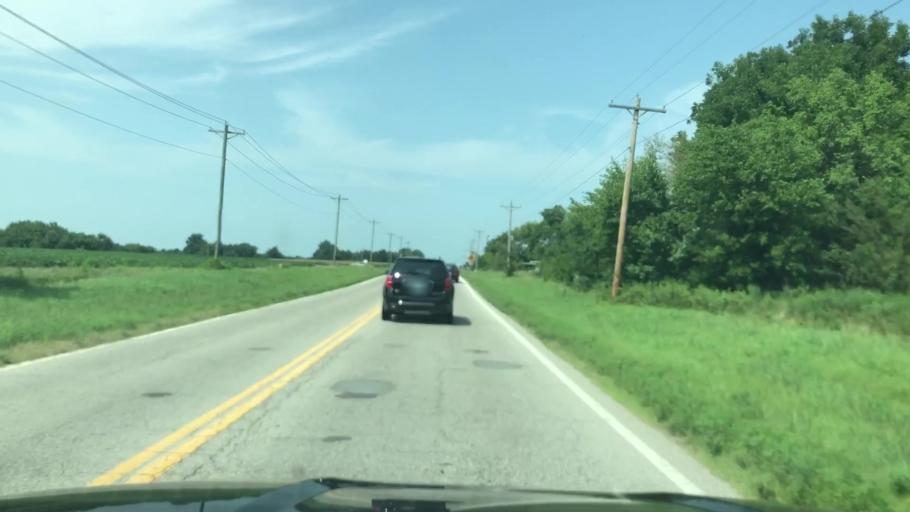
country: US
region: Oklahoma
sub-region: Ottawa County
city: Miami
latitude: 36.8971
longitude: -94.8418
